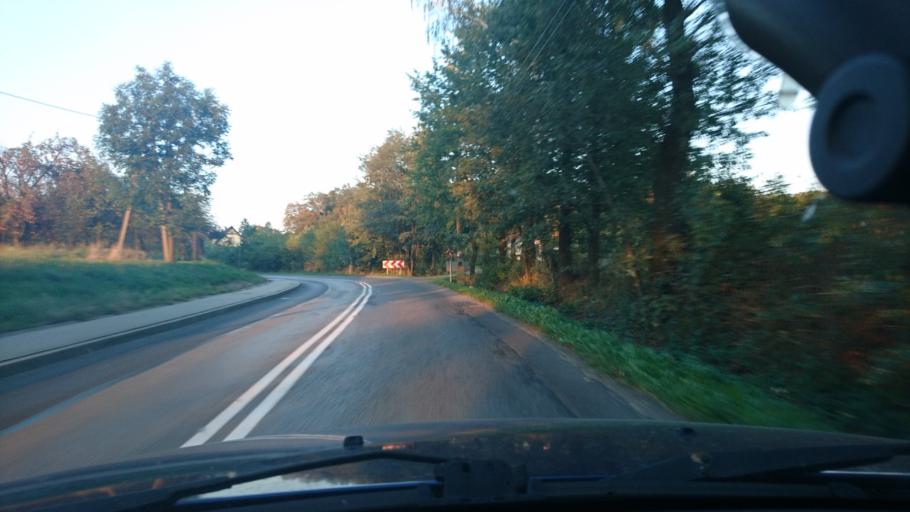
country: PL
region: Silesian Voivodeship
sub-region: Powiat bielski
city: Bestwina
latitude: 49.8993
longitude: 19.0728
